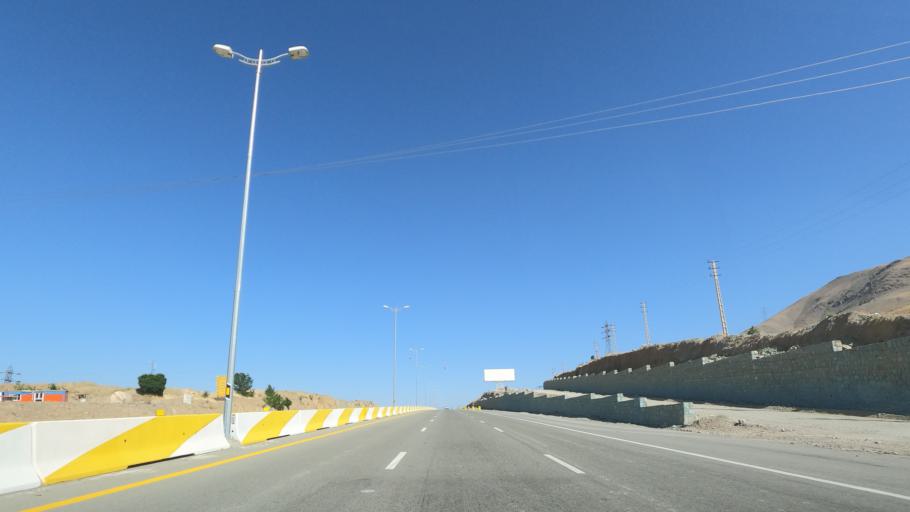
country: IR
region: Tehran
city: Shahr-e Qods
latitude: 35.7650
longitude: 51.0692
